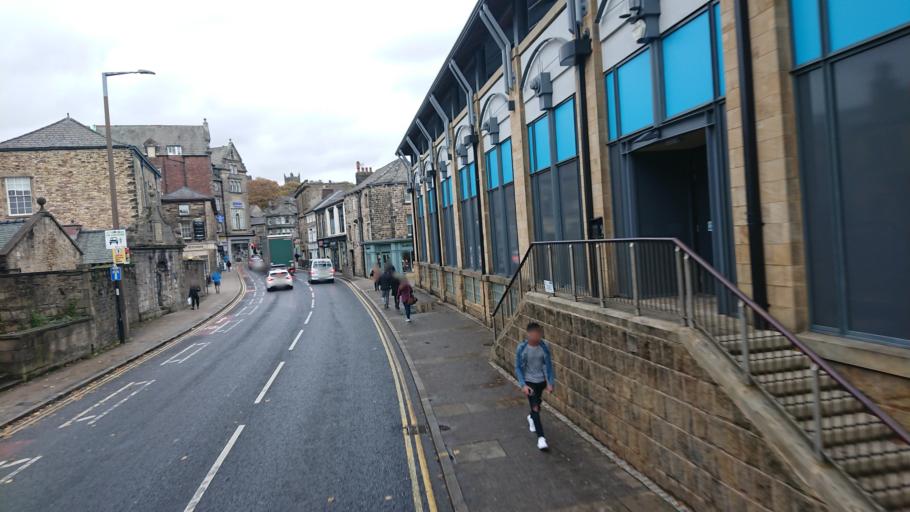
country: GB
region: England
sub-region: Lancashire
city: Lancaster
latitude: 54.0477
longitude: -2.8020
